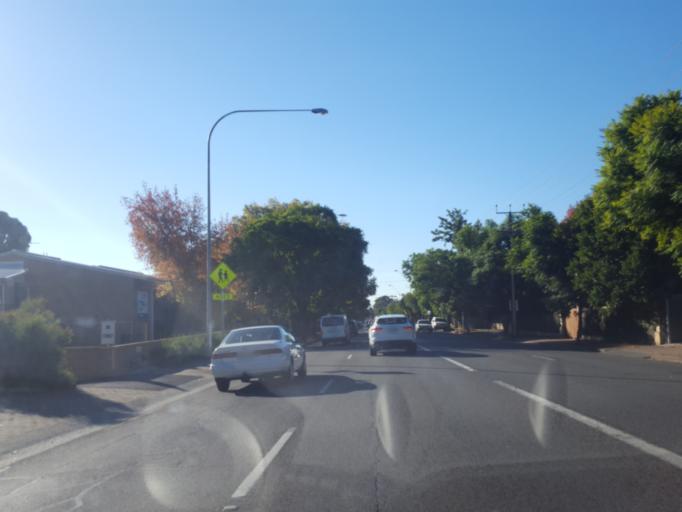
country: AU
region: South Australia
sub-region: Unley
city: Fullarton
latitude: -34.9533
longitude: 138.6255
